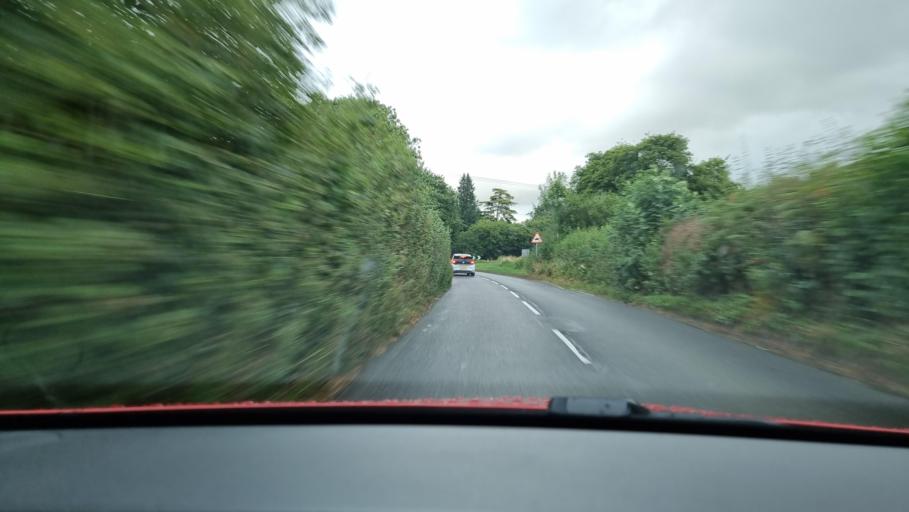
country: GB
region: England
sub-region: Buckinghamshire
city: Chesham
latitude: 51.7196
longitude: -0.5846
